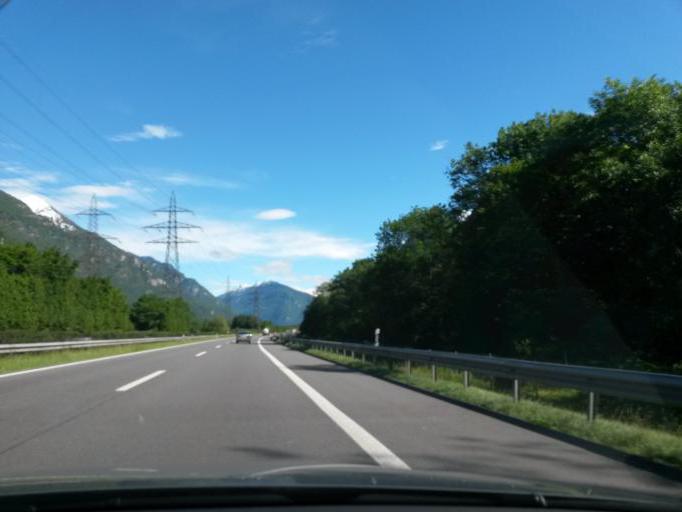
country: CH
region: Ticino
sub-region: Riviera District
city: Claro
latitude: 46.2479
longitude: 9.0124
